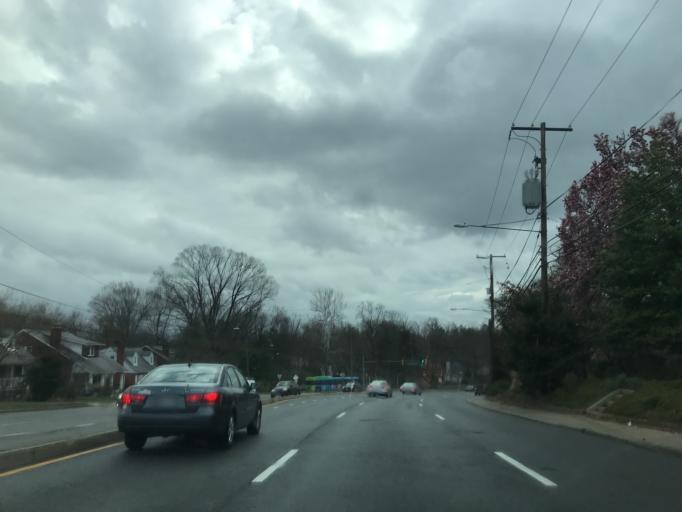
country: US
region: Maryland
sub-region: Montgomery County
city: Four Corners
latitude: 39.0100
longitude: -77.0177
